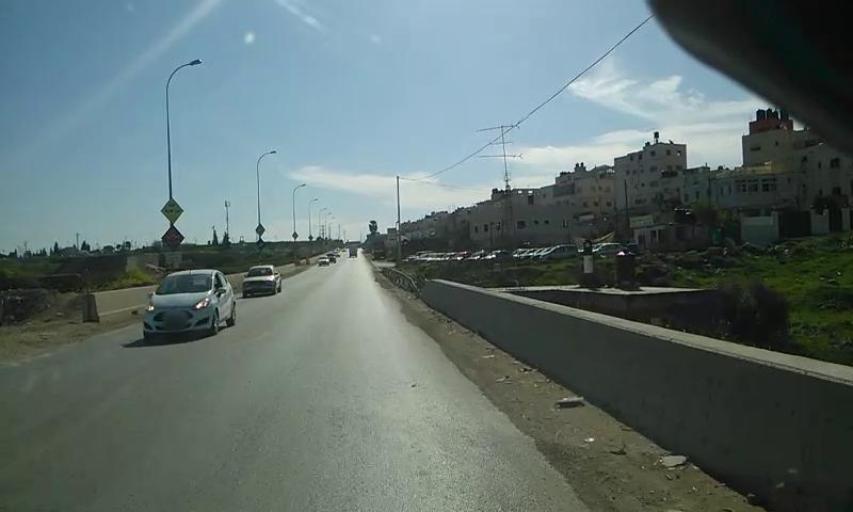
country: PS
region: West Bank
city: Ar Ram wa Dahiyat al Barid
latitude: 31.8574
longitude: 35.2377
